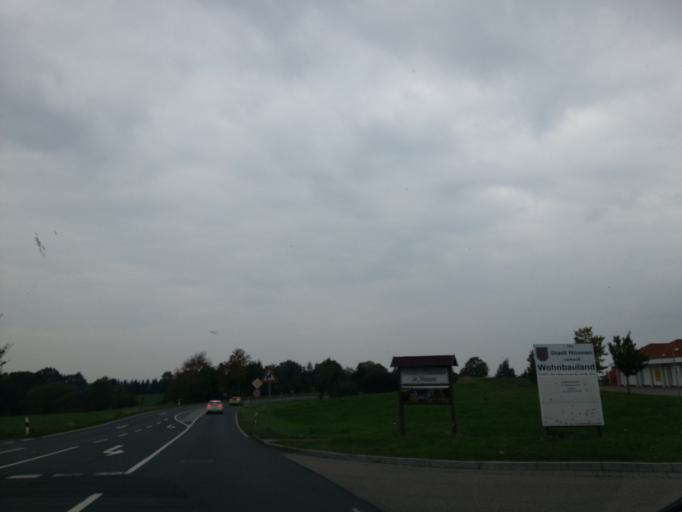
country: DE
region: Saxony
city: Nossen
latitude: 51.0490
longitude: 13.2908
